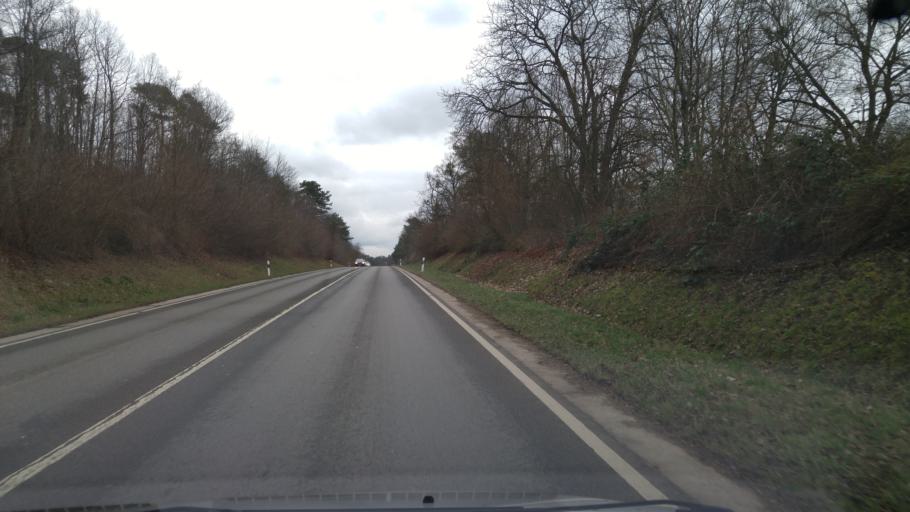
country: DE
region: Baden-Wuerttemberg
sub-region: Regierungsbezirk Stuttgart
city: Leonberg
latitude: 48.7956
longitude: 9.0342
